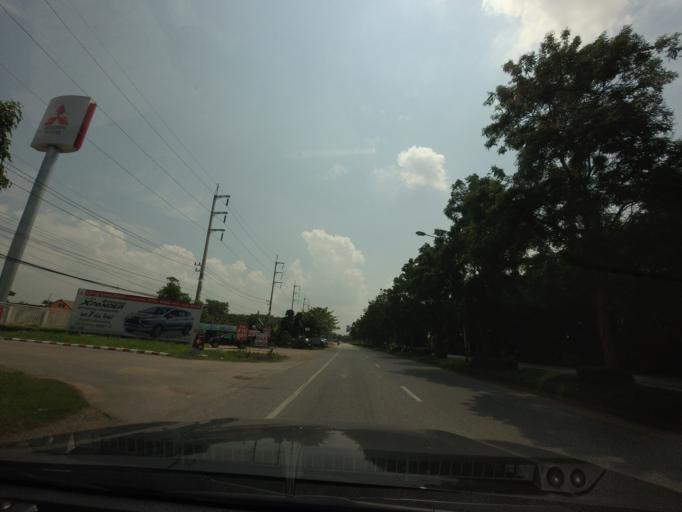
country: TH
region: Uttaradit
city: Uttaradit
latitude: 17.6005
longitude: 100.1252
